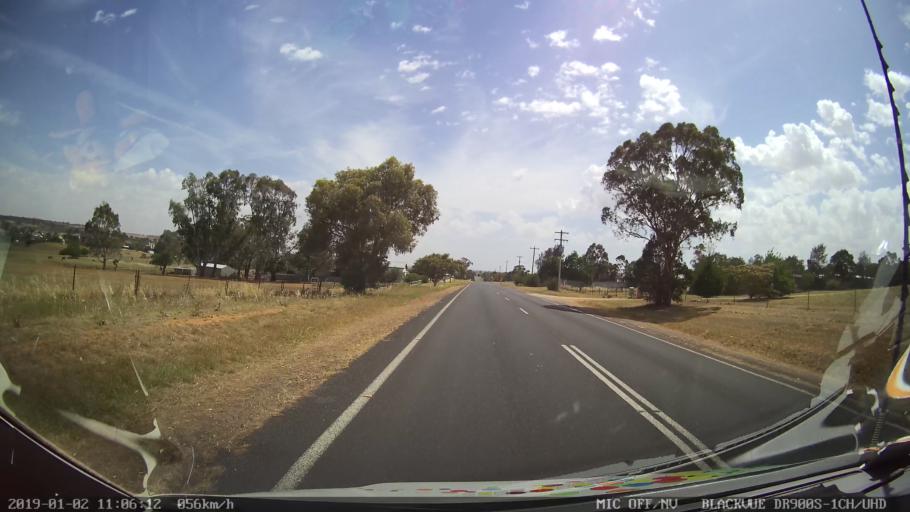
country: AU
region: New South Wales
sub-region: Young
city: Young
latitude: -34.5570
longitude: 148.3557
